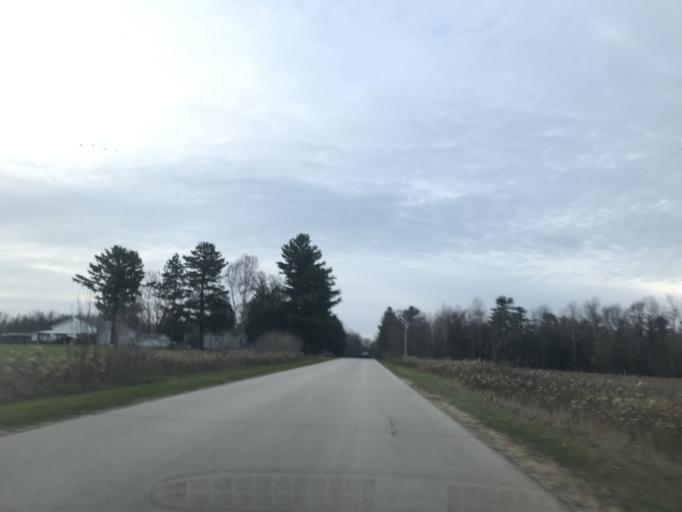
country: US
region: Wisconsin
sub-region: Marinette County
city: Peshtigo
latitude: 45.0681
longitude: -87.7995
